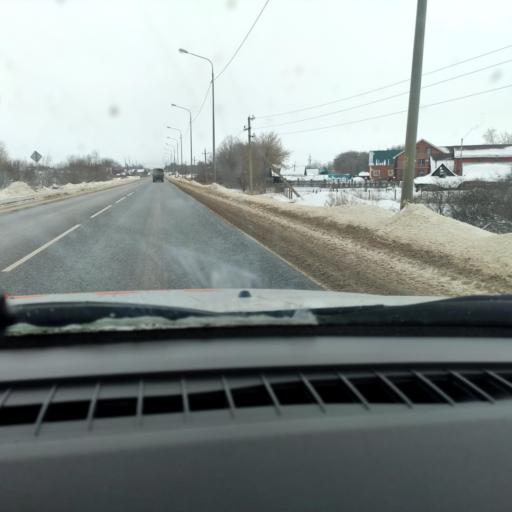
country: RU
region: Samara
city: Dubovyy Umet
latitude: 52.9648
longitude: 50.2853
